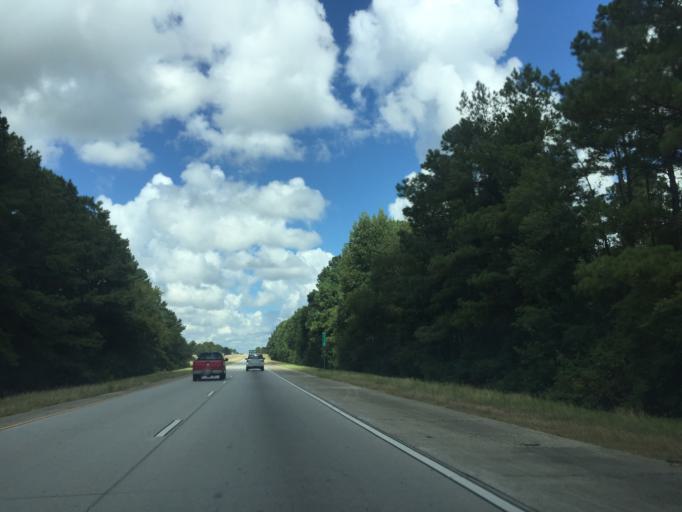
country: US
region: Georgia
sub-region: Candler County
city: Metter
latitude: 32.3464
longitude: -81.9685
